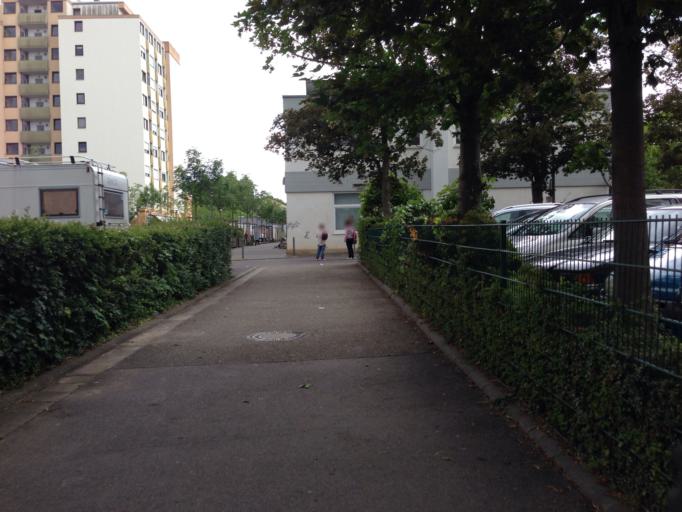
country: DE
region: Hesse
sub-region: Regierungsbezirk Darmstadt
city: Hanau am Main
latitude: 50.1317
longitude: 8.8854
